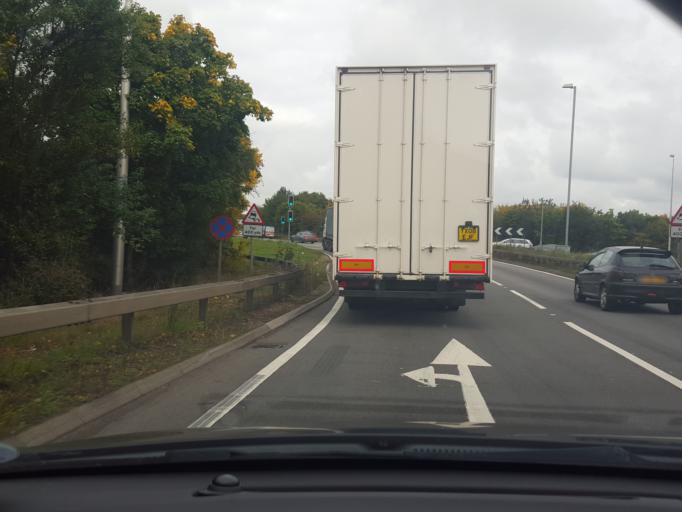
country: GB
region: England
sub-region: Suffolk
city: Bramford
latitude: 52.0348
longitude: 1.0972
